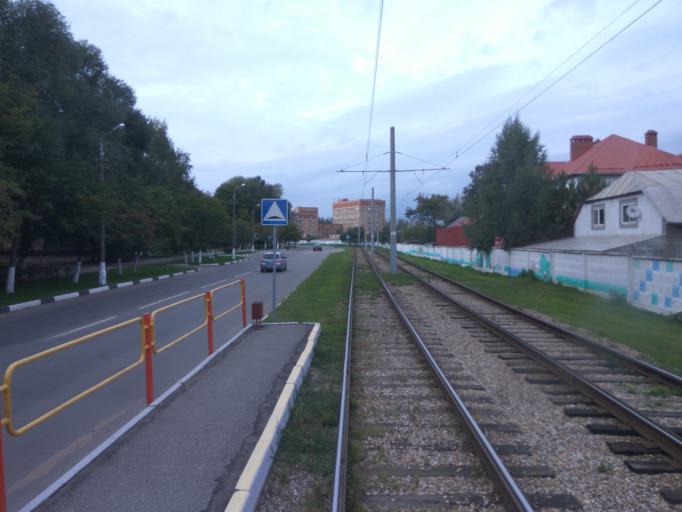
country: RU
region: Moskovskaya
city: Kolomna
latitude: 55.0640
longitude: 38.7567
